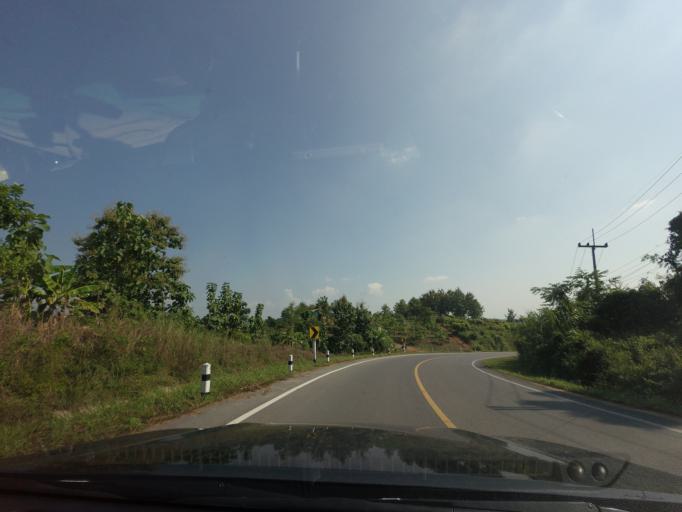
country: TH
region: Nan
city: Santi Suk
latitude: 18.8961
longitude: 100.8392
